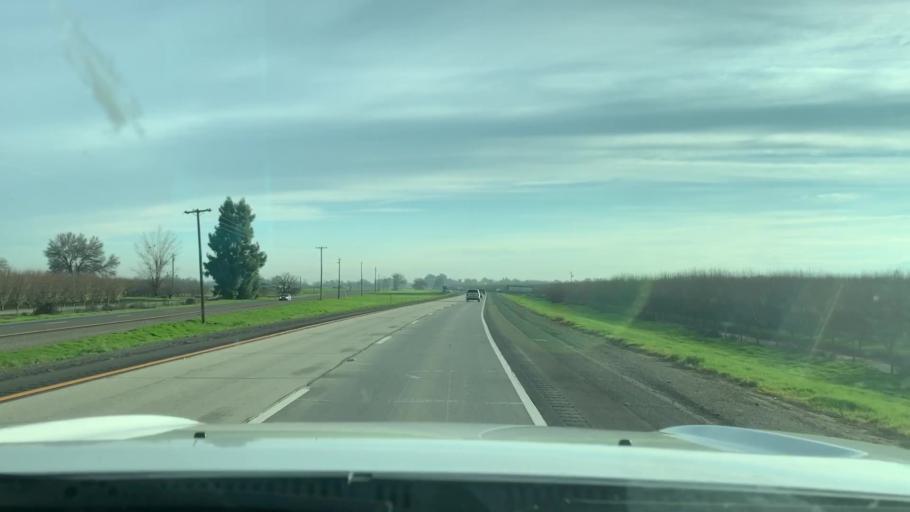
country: US
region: California
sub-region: Fresno County
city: Riverdale
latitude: 36.3836
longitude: -119.8098
